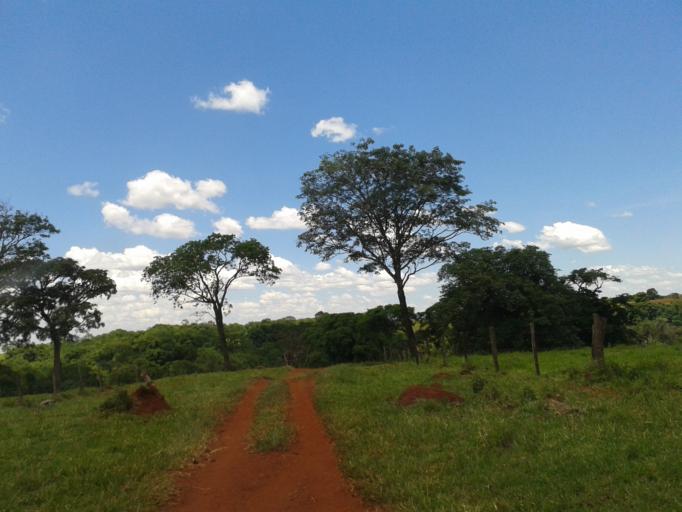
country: BR
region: Minas Gerais
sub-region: Centralina
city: Centralina
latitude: -18.7029
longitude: -49.1768
